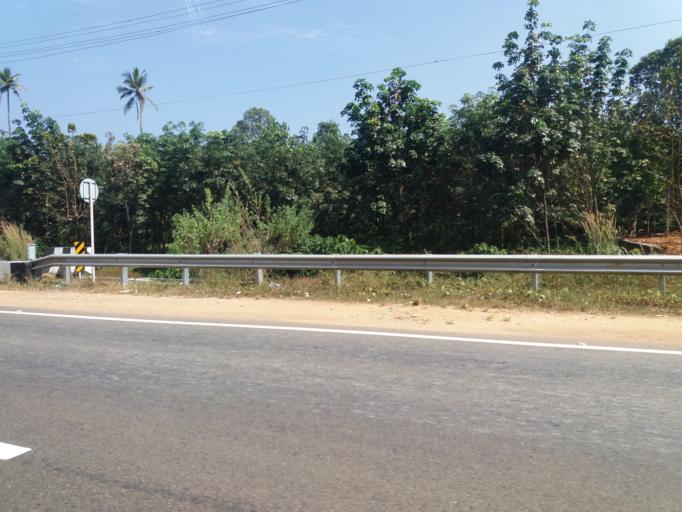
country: IN
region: Kerala
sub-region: Kottayam
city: Palackattumala
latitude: 9.8627
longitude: 76.6974
